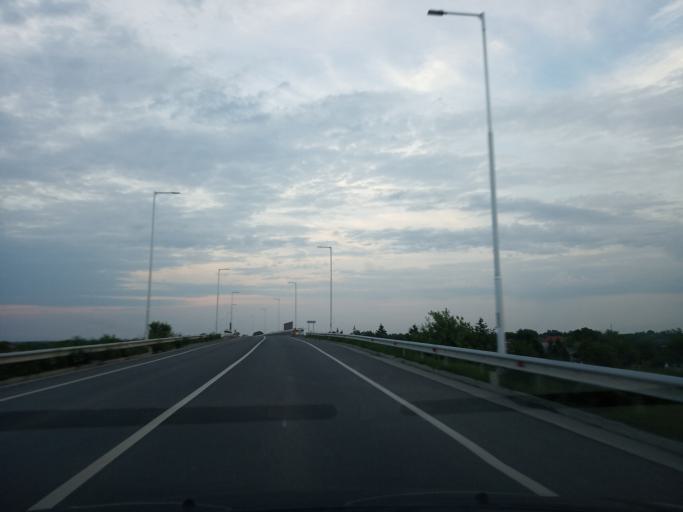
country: RO
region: Timis
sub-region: Comuna Voiteg
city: Voiteg
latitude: 45.4630
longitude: 21.2354
